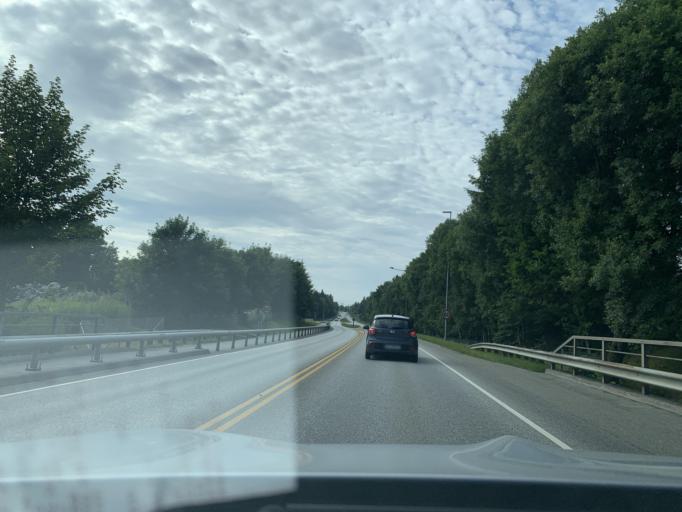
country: NO
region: Rogaland
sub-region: Stavanger
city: Stavanger
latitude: 58.9157
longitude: 5.7212
